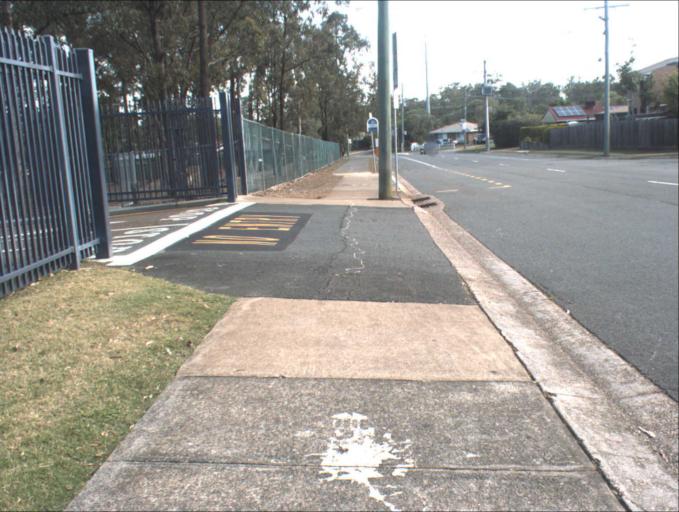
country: AU
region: Queensland
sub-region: Logan
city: Logan City
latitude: -27.6605
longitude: 153.0984
